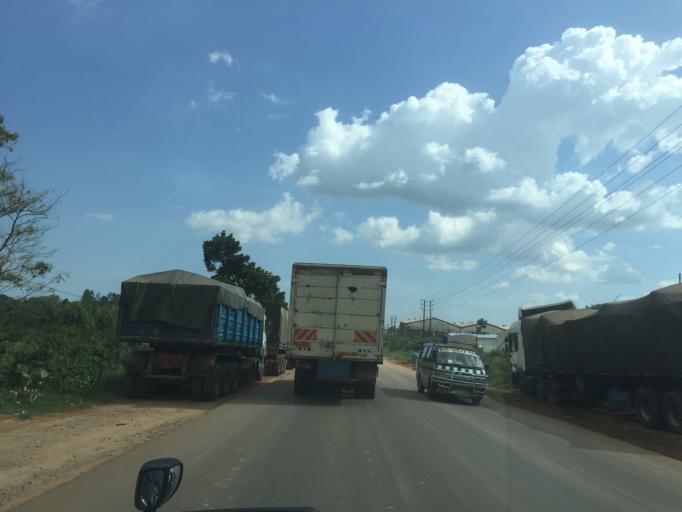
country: UG
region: Central Region
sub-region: Wakiso District
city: Wakiso
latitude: 0.4956
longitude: 32.5227
